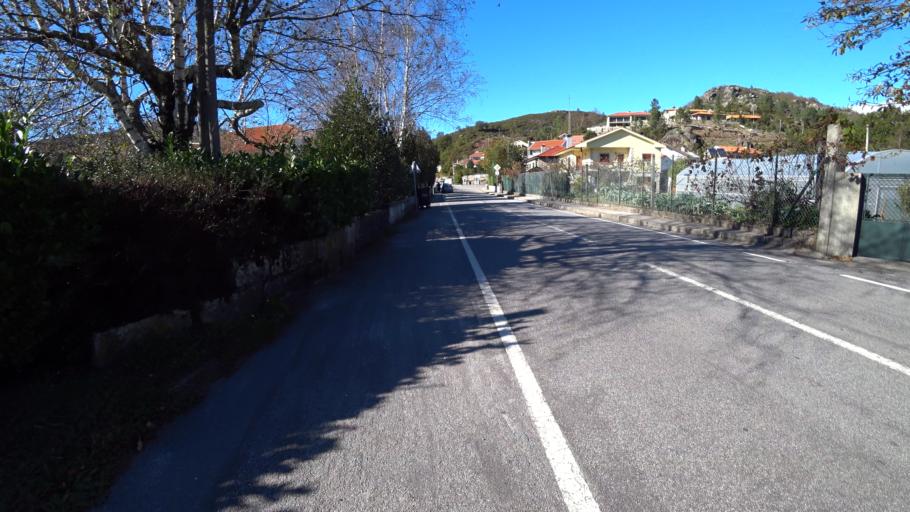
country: PT
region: Braga
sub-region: Terras de Bouro
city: Antas
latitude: 41.7575
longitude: -8.1931
